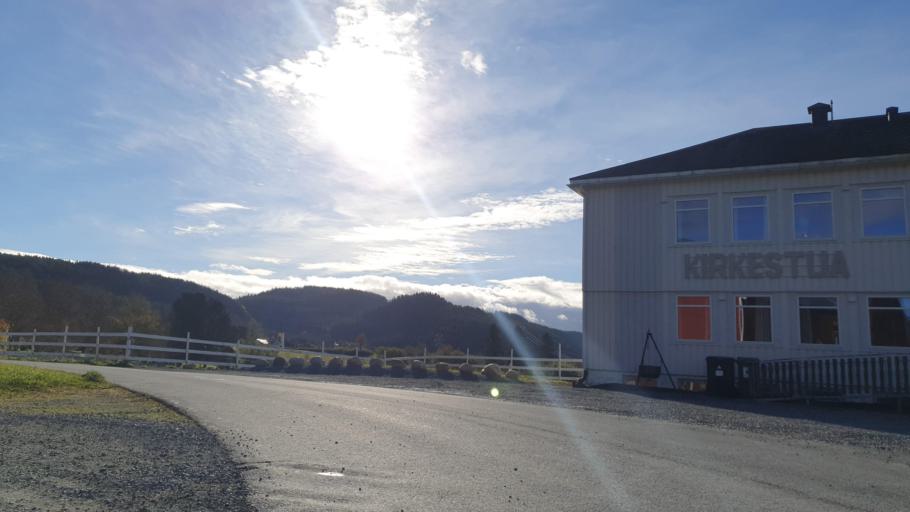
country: NO
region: Sor-Trondelag
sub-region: Klaebu
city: Klaebu
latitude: 63.2961
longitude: 10.4742
